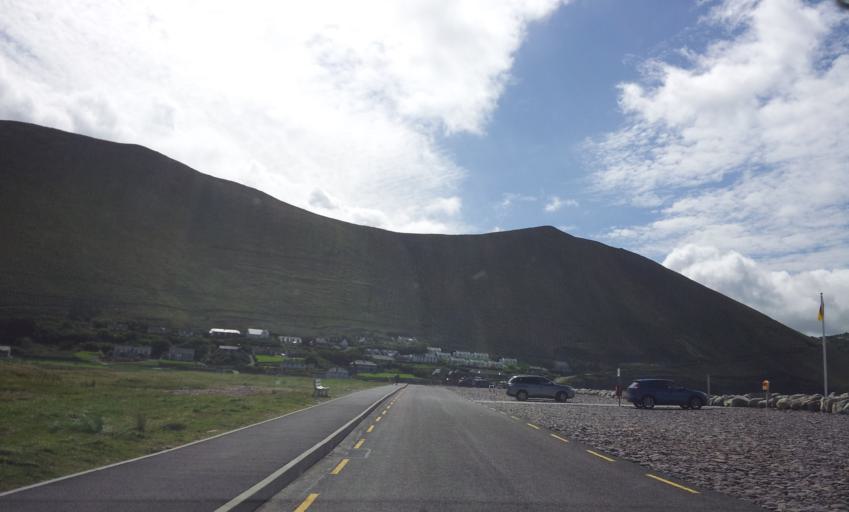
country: IE
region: Munster
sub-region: Ciarrai
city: Killorglin
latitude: 52.0584
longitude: -9.9745
